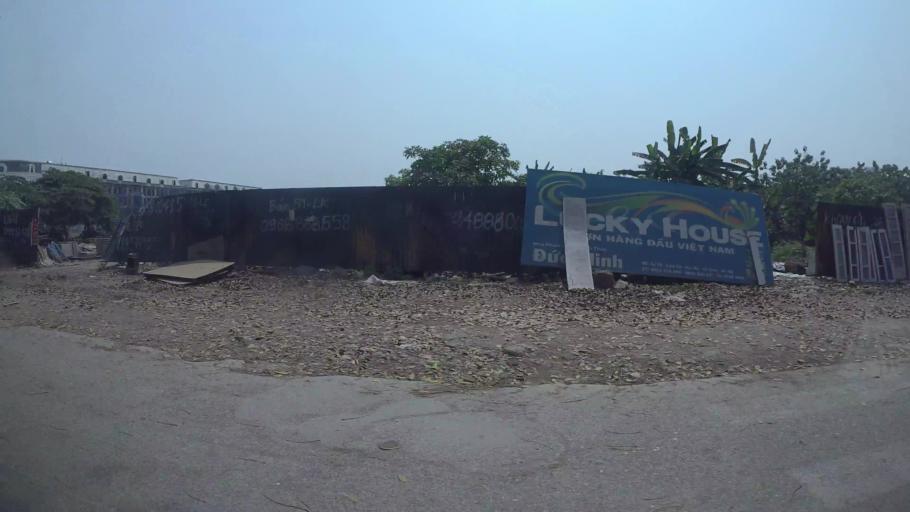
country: VN
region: Ha Noi
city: Ha Dong
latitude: 20.9903
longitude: 105.7639
